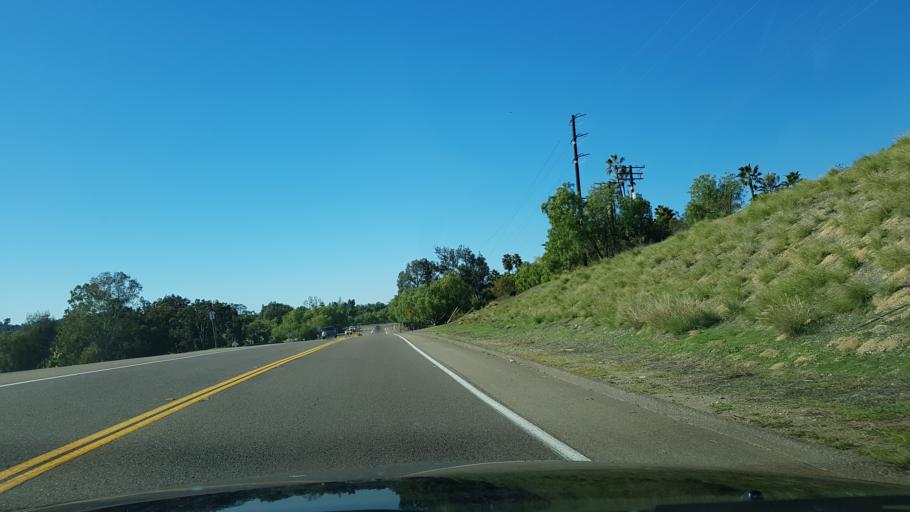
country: US
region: California
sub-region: San Diego County
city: Rancho Santa Fe
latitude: 33.0351
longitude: -117.1698
